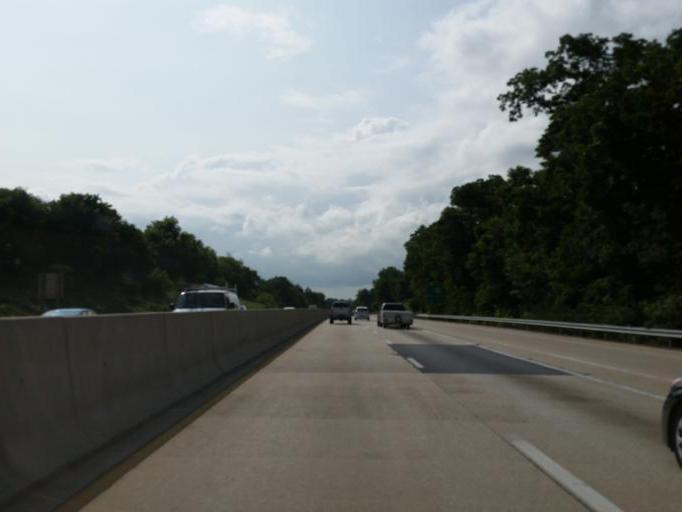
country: US
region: Pennsylvania
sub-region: Lancaster County
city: Salunga
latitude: 40.1070
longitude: -76.4319
